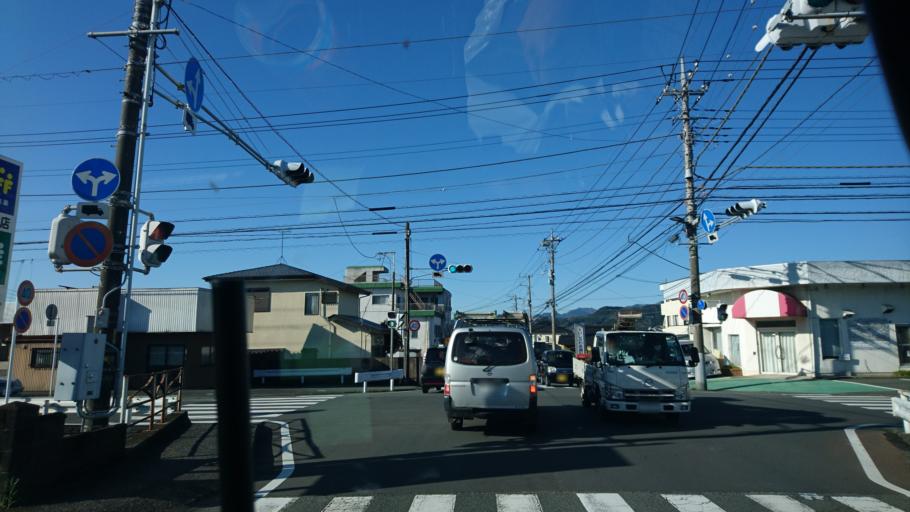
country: JP
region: Shizuoka
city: Fujinomiya
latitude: 35.2368
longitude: 138.6156
